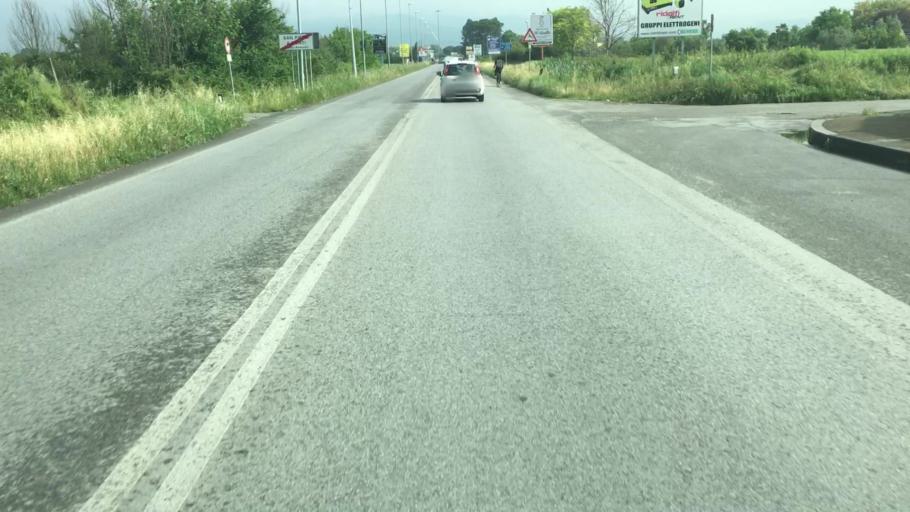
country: IT
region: Tuscany
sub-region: Province of Florence
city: San Mauro
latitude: 43.8100
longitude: 11.1184
